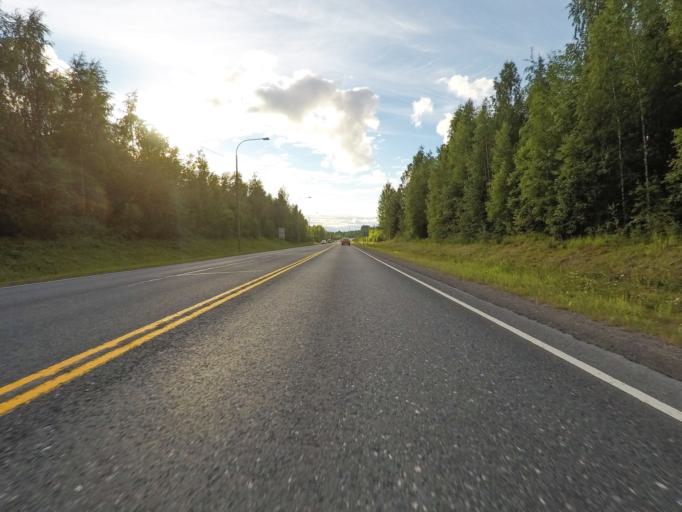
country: FI
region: Northern Savo
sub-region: Kuopio
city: Kuopio
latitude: 62.9555
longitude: 27.8683
